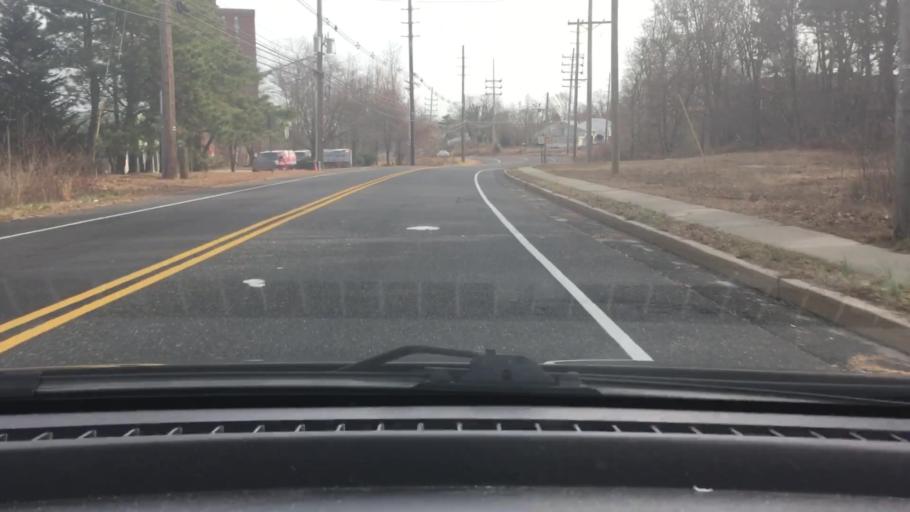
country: US
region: New Jersey
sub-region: Monmouth County
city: Wanamassa
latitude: 40.2179
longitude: -74.0433
